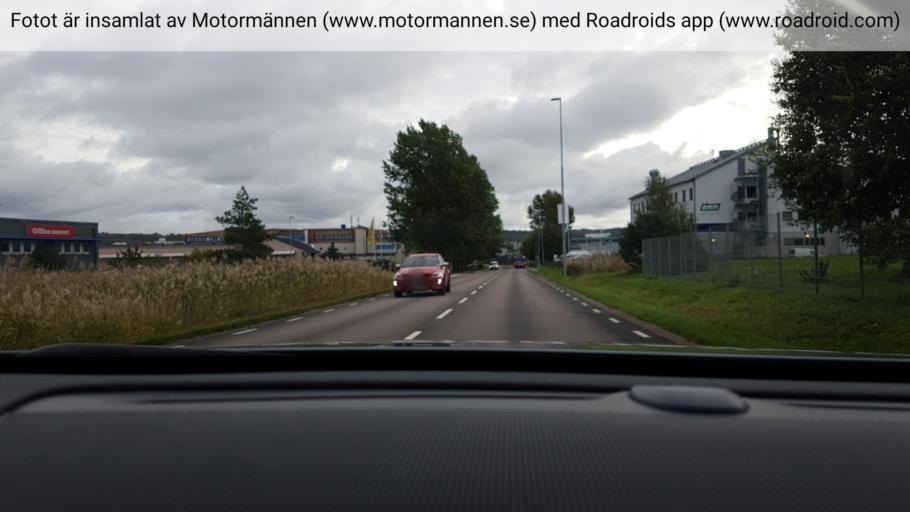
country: SE
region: Vaestra Goetaland
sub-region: Molndal
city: Moelndal
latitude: 57.6405
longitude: 12.0060
